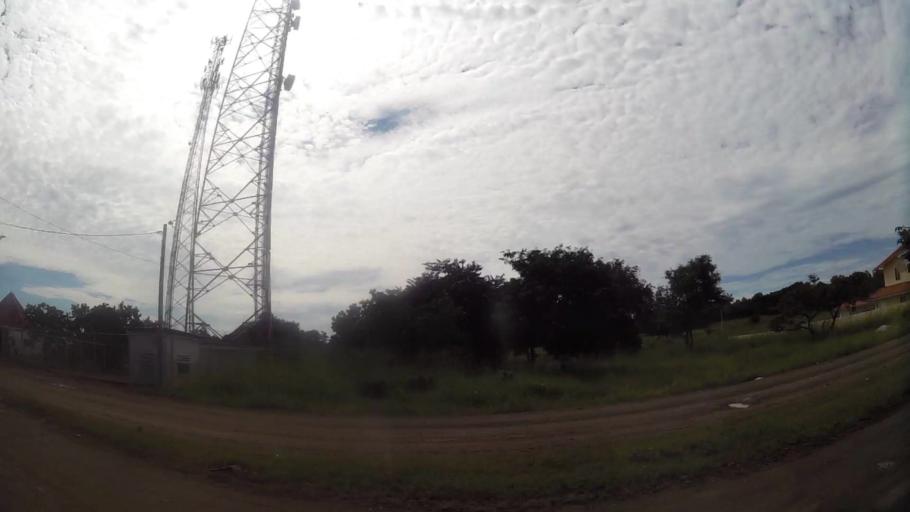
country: PA
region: Panama
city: Nueva Gorgona
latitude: 8.5469
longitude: -79.8860
